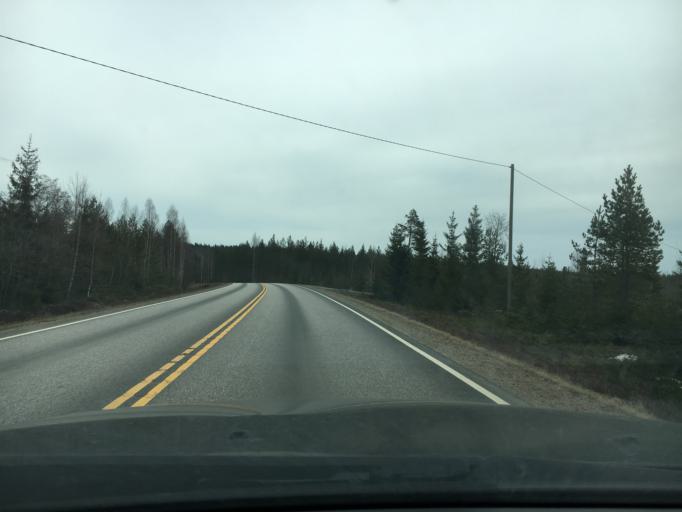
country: FI
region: Central Finland
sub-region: AEaenekoski
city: Sumiainen
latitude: 62.5790
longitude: 26.1150
